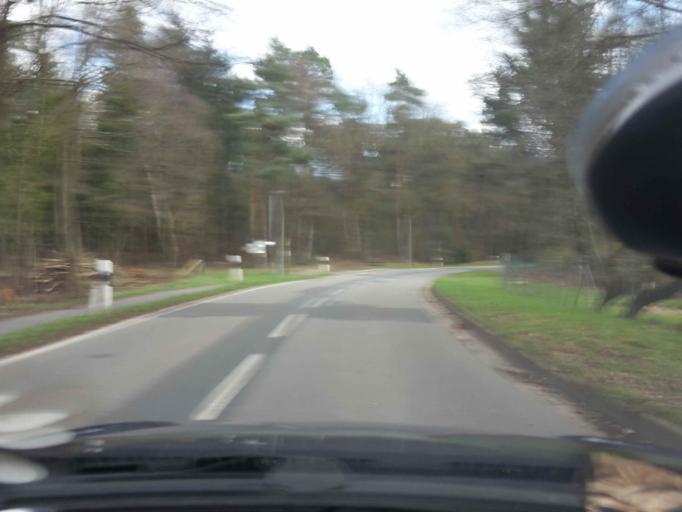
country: DE
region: Lower Saxony
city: Jesteburg
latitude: 53.2856
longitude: 9.9148
